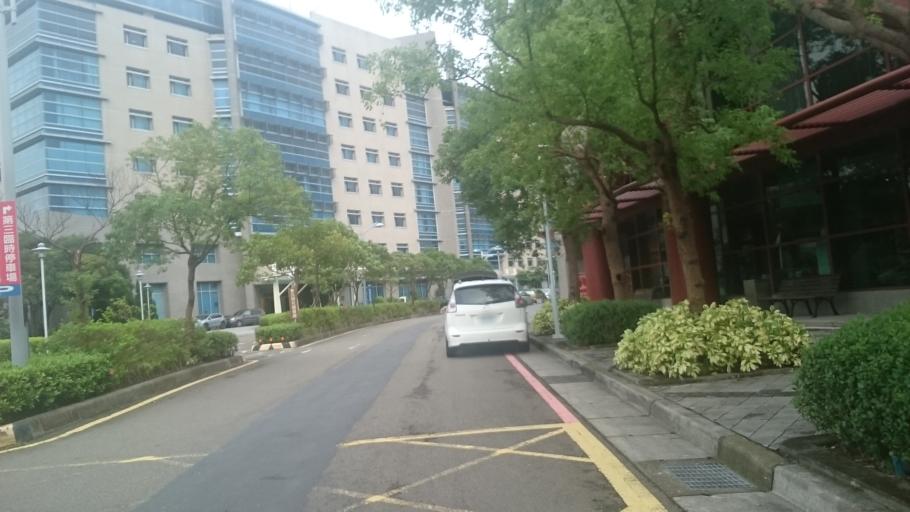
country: TW
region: Taiwan
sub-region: Hsinchu
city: Zhubei
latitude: 24.8429
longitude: 121.0156
